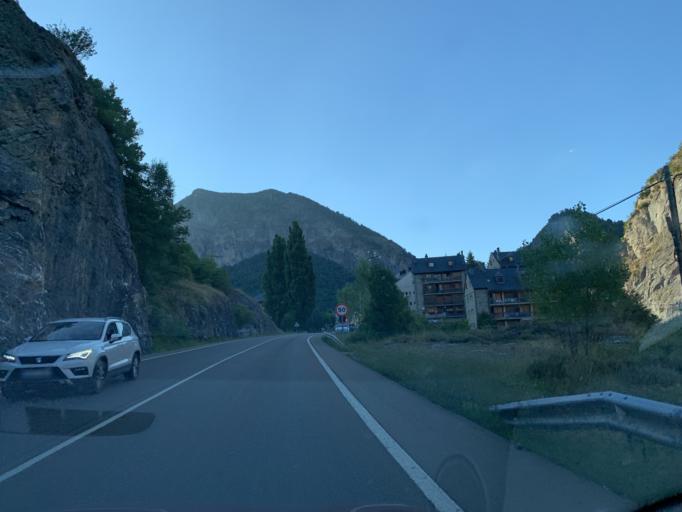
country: ES
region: Aragon
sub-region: Provincia de Huesca
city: Hoz de Jaca
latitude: 42.7306
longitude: -0.3099
